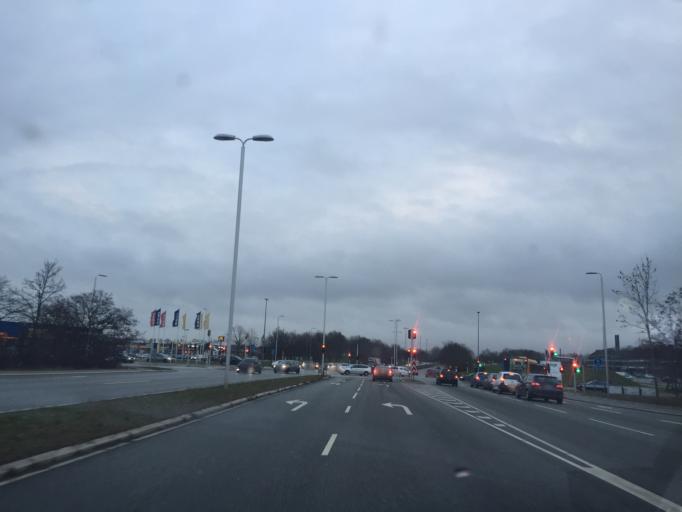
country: DK
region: Capital Region
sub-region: Hoje-Taastrup Kommune
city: Taastrup
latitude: 55.6614
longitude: 12.2823
